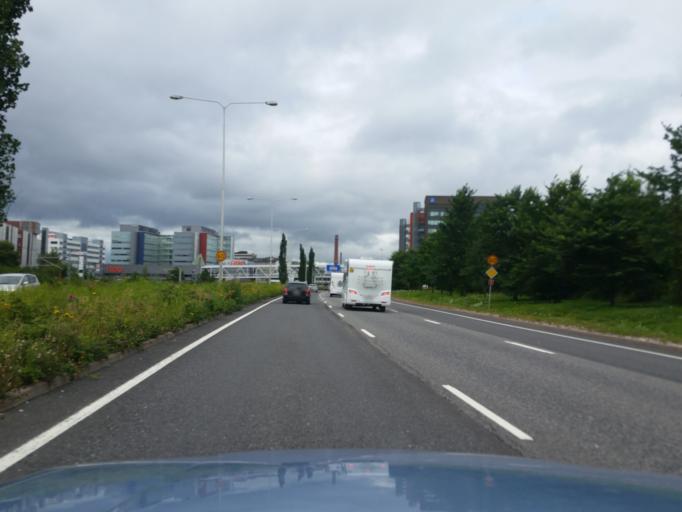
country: FI
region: Varsinais-Suomi
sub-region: Turku
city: Turku
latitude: 60.4476
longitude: 22.3024
